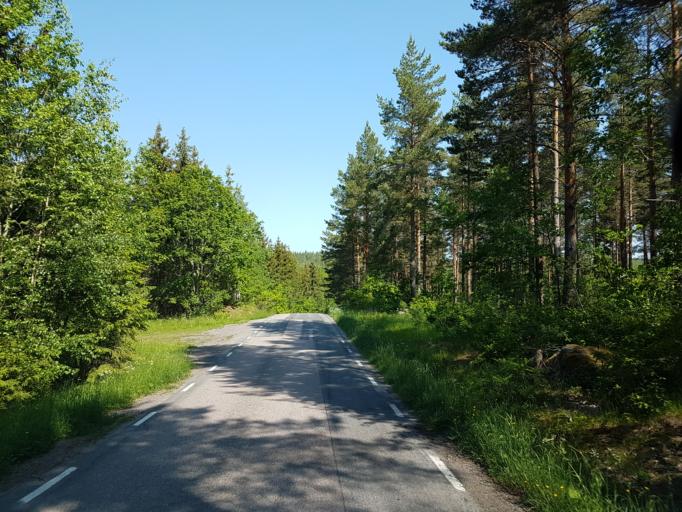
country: SE
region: OEstergoetland
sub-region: Atvidabergs Kommun
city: Atvidaberg
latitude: 58.2621
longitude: 16.2062
